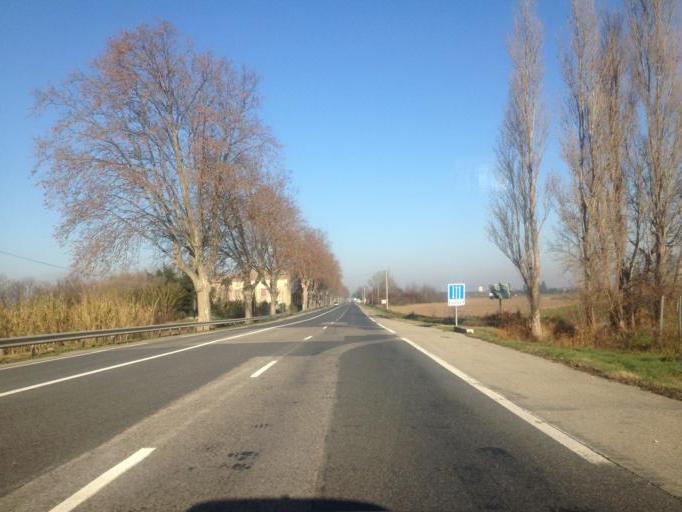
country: FR
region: Provence-Alpes-Cote d'Azur
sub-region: Departement du Vaucluse
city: Lapalud
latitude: 44.2847
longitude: 4.6952
